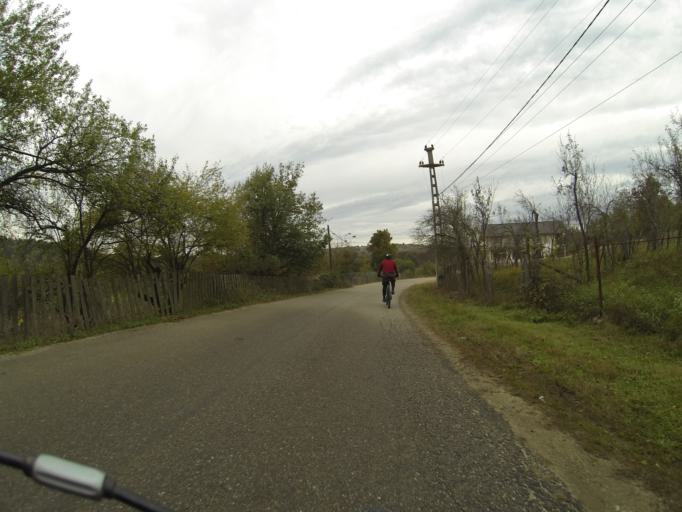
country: RO
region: Gorj
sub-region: Comuna Tismana
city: Sohodol
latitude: 45.0432
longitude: 22.8989
